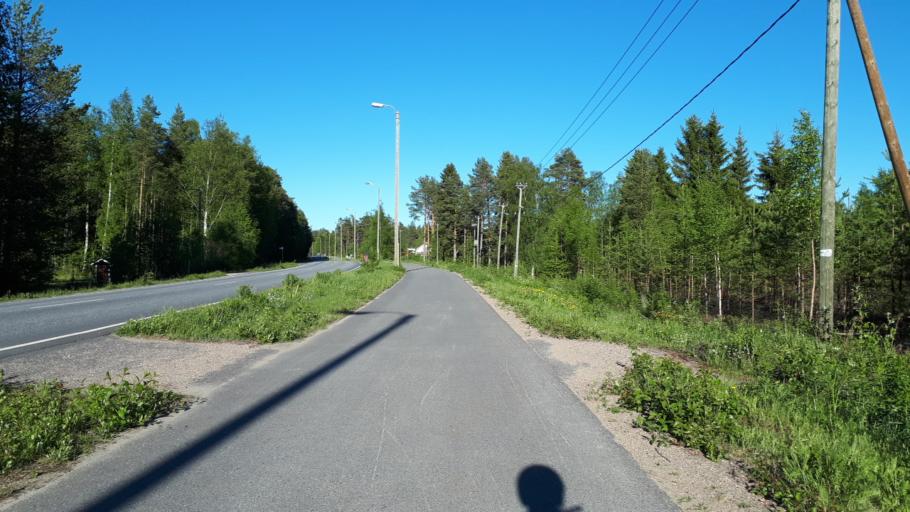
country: FI
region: Northern Ostrobothnia
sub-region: Oulunkaari
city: Ii
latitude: 65.3249
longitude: 25.5041
